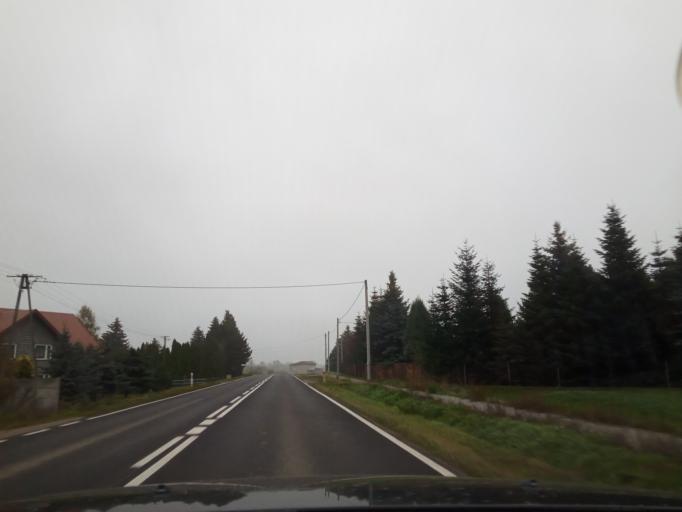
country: PL
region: Lesser Poland Voivodeship
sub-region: Powiat proszowicki
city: Proszowice
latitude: 50.1708
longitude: 20.2248
